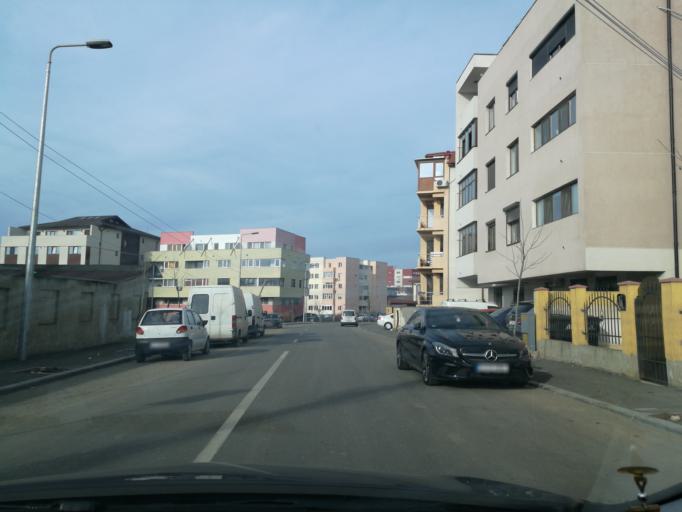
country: RO
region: Constanta
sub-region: Municipiul Constanta
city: Constanta
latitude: 44.1846
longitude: 28.6112
